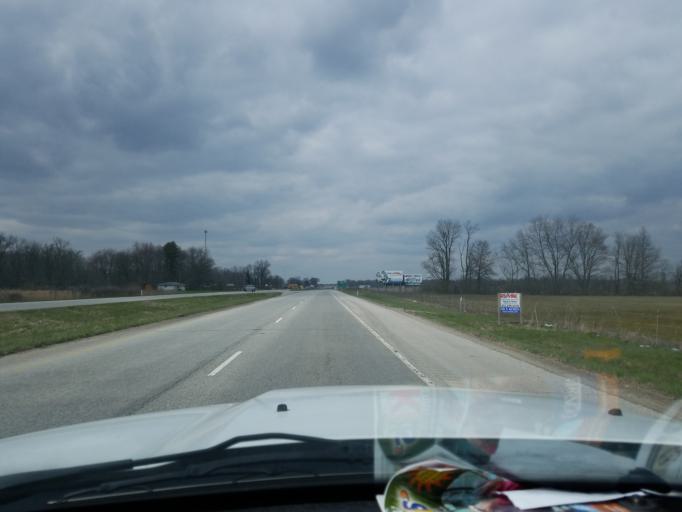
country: US
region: Indiana
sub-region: Sullivan County
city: Farmersburg
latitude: 39.3492
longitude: -87.3882
